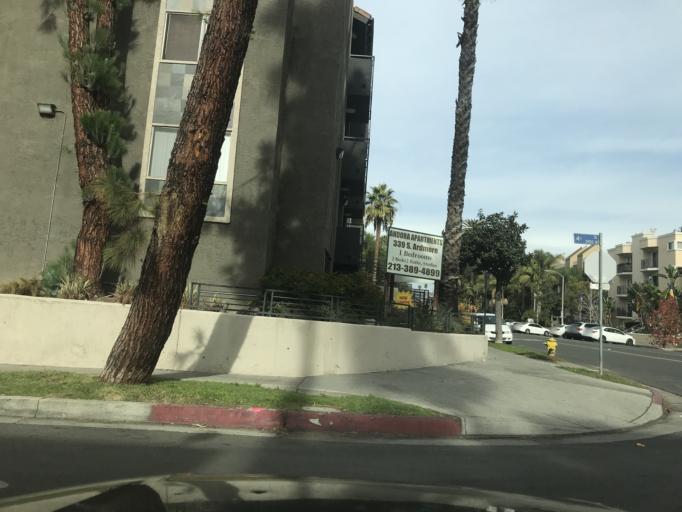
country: US
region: California
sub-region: Los Angeles County
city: Silver Lake
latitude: 34.0672
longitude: -118.3018
